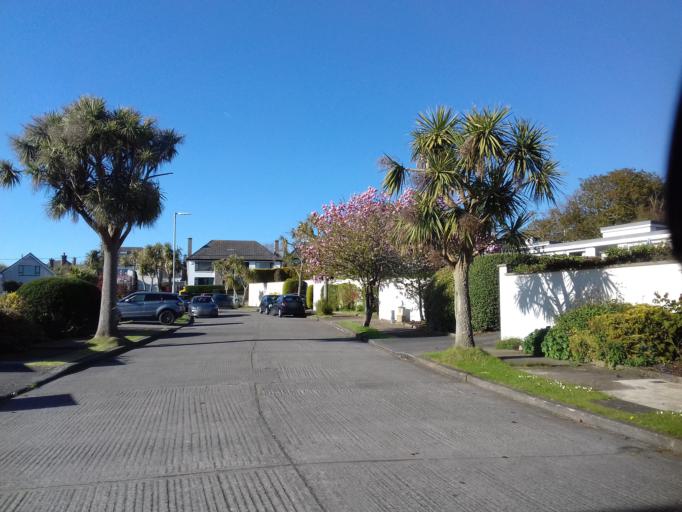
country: IE
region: Leinster
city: Sutton
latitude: 53.3726
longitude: -6.0960
